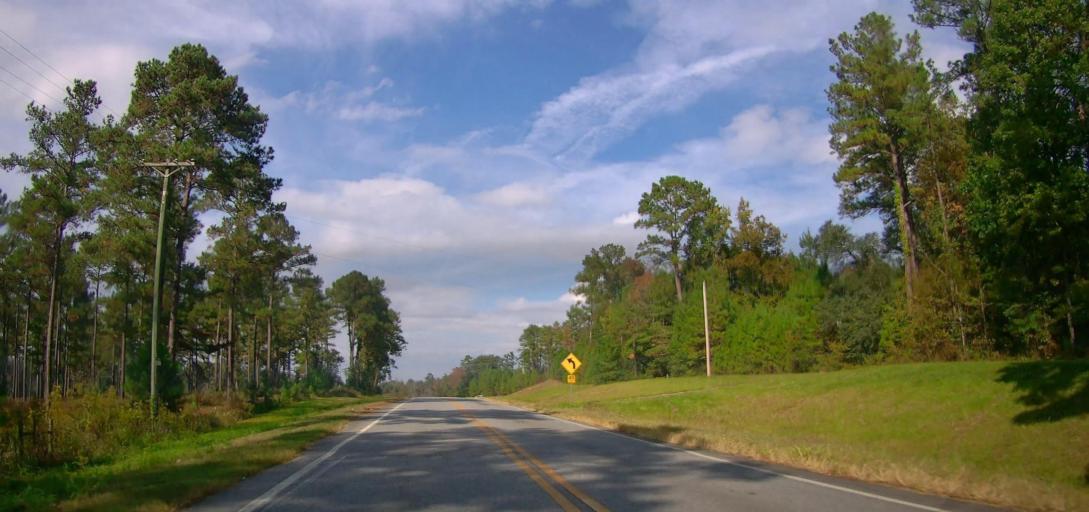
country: US
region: Georgia
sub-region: Thomas County
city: Thomasville
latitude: 30.9056
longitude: -84.0061
